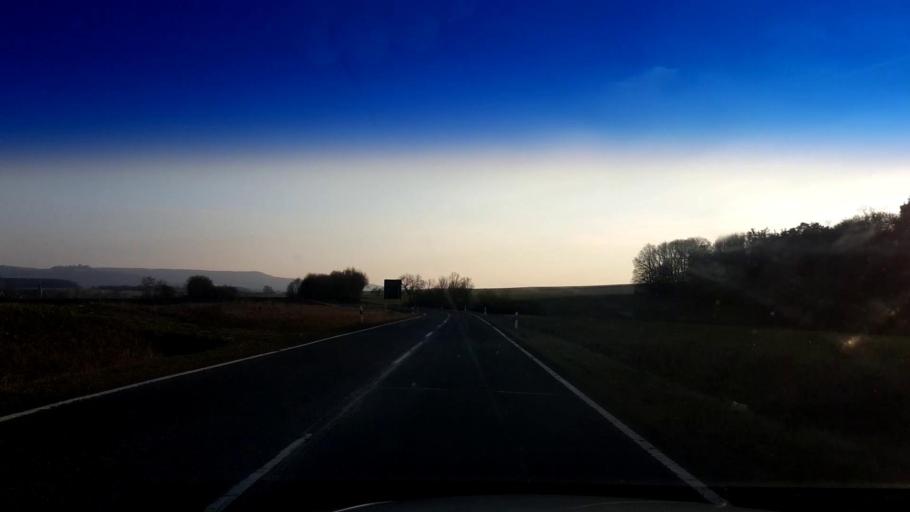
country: DE
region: Bavaria
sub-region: Upper Franconia
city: Schesslitz
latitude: 50.0141
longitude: 11.0110
